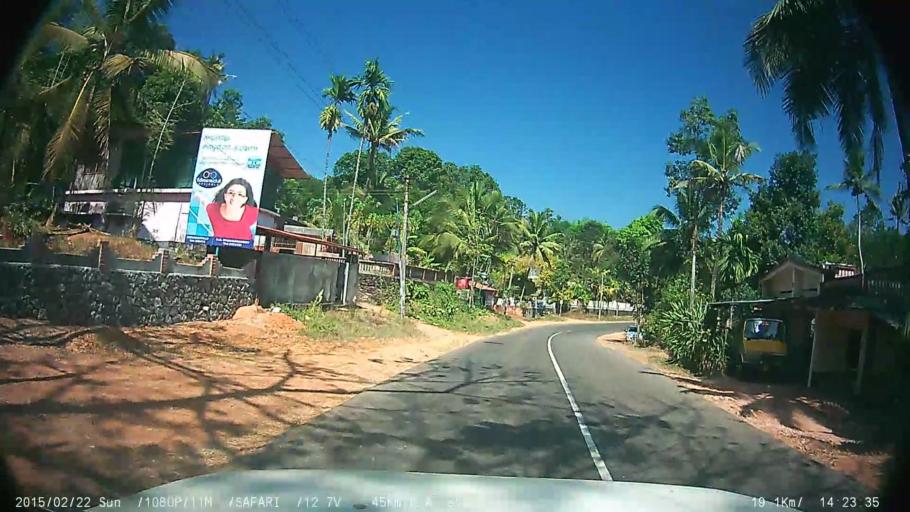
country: IN
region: Kerala
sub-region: Kottayam
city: Lalam
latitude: 9.5675
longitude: 76.7110
